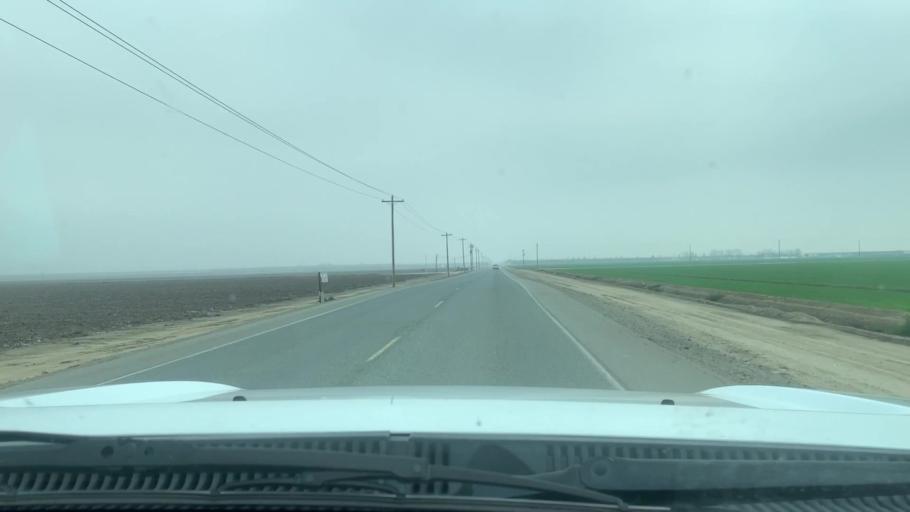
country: US
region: California
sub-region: Kern County
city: Buttonwillow
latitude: 35.5004
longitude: -119.4697
